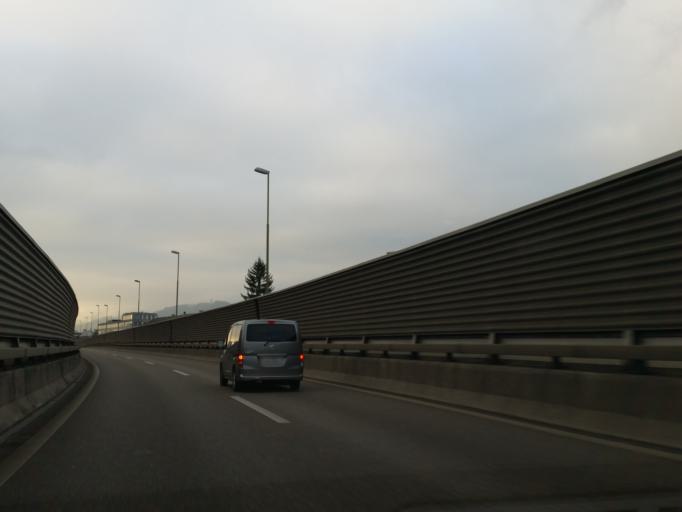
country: CH
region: Zurich
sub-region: Bezirk Zuerich
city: Zuerich (Kreis 4) / Werd
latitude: 47.3661
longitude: 8.5227
